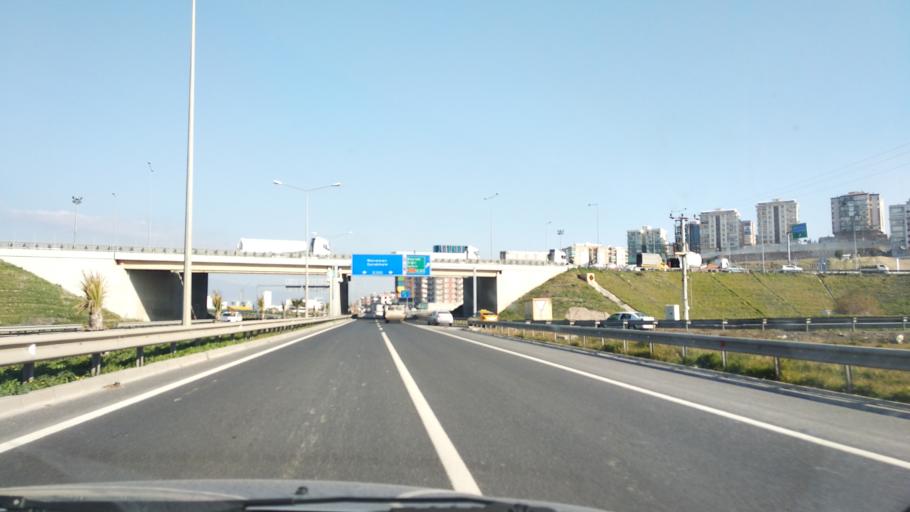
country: TR
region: Izmir
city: Menemen
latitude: 38.5700
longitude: 27.0560
